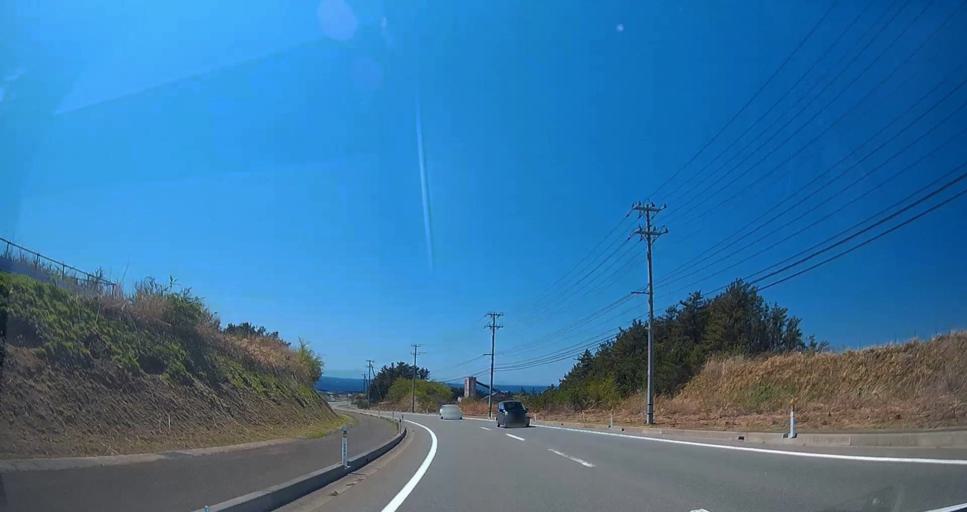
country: JP
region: Hokkaido
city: Hakodate
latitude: 41.5202
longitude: 140.9110
